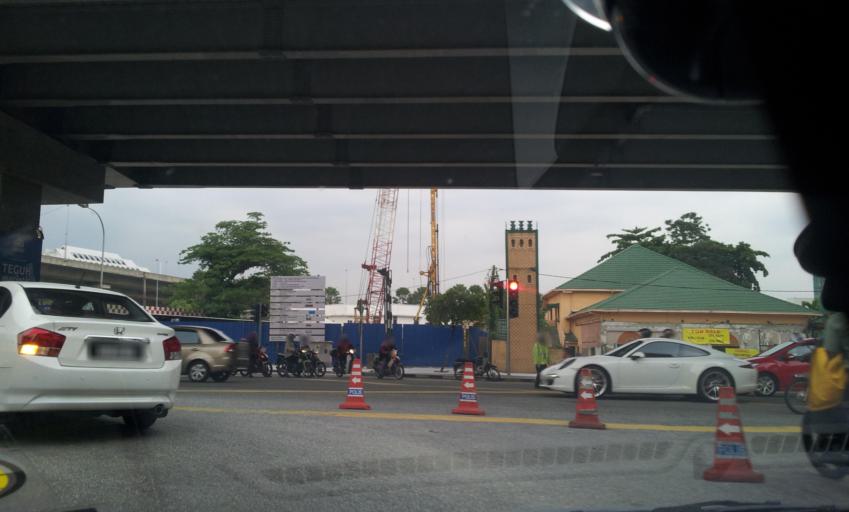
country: MY
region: Kuala Lumpur
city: Kuala Lumpur
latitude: 3.1639
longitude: 101.7159
